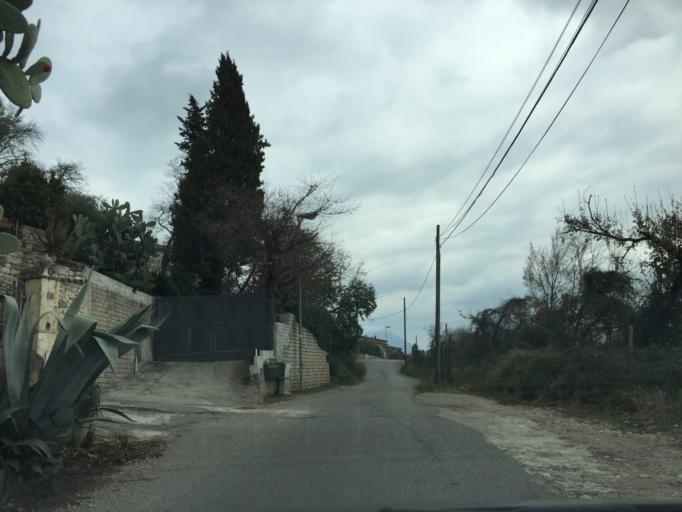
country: IT
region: Latium
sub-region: Provincia di Frosinone
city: Cassino
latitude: 41.4815
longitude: 13.8103
